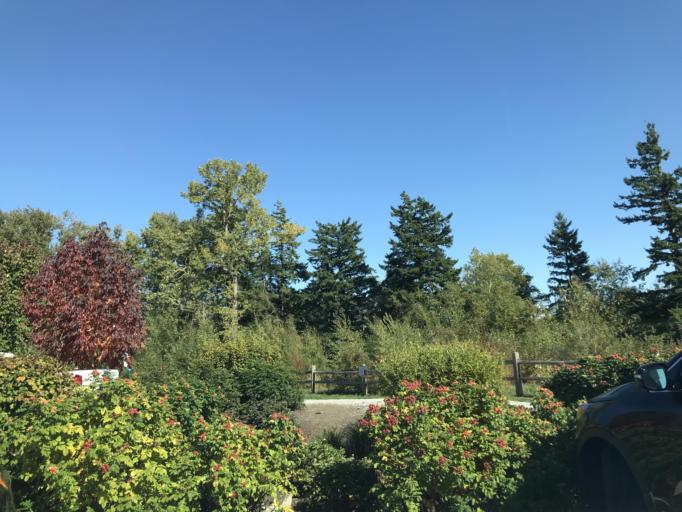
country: US
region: Washington
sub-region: Whatcom County
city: Bellingham
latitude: 48.8001
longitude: -122.4925
